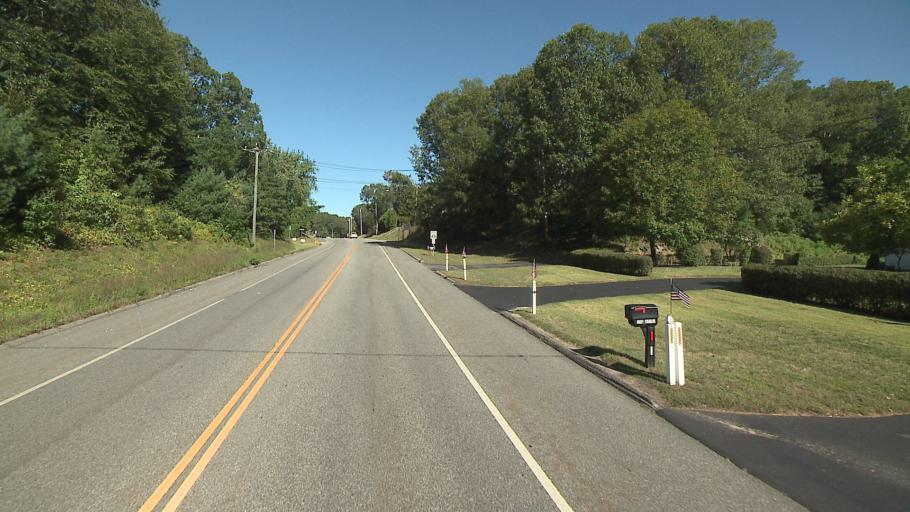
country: US
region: Connecticut
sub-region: New London County
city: Gales Ferry
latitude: 41.4728
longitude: -72.0618
